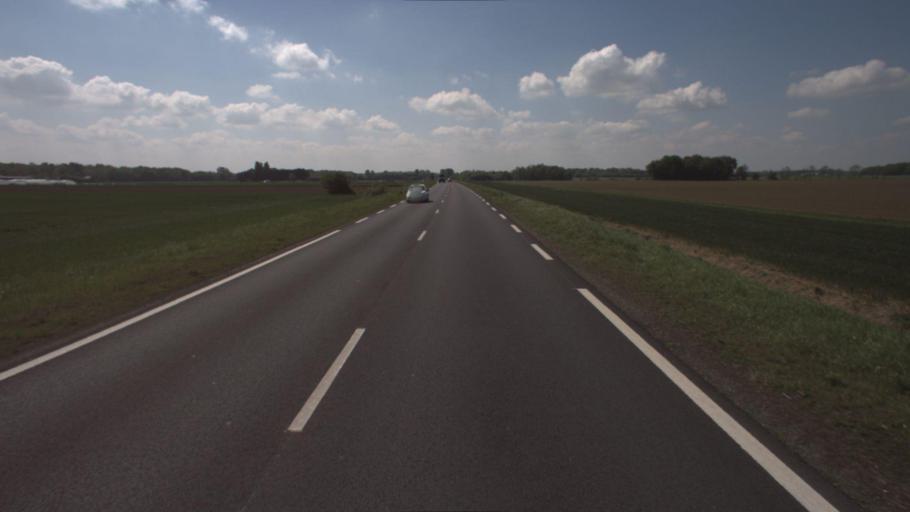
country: FR
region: Ile-de-France
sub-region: Departement de Seine-et-Marne
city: La Houssaye-en-Brie
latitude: 48.7591
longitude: 2.8594
